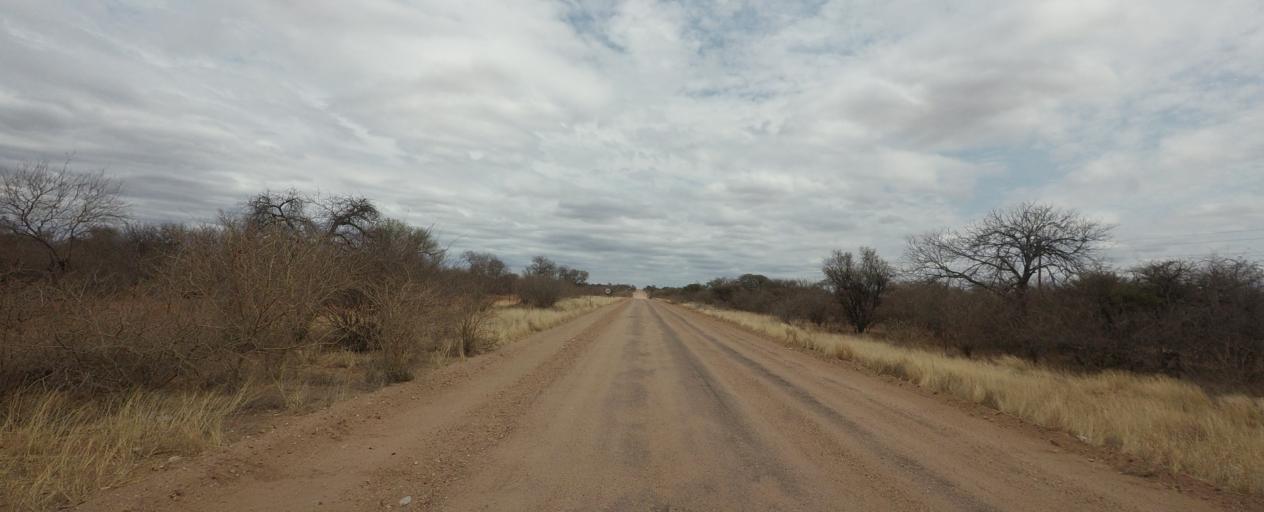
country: BW
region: Central
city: Mathathane
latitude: -22.6744
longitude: 28.6747
